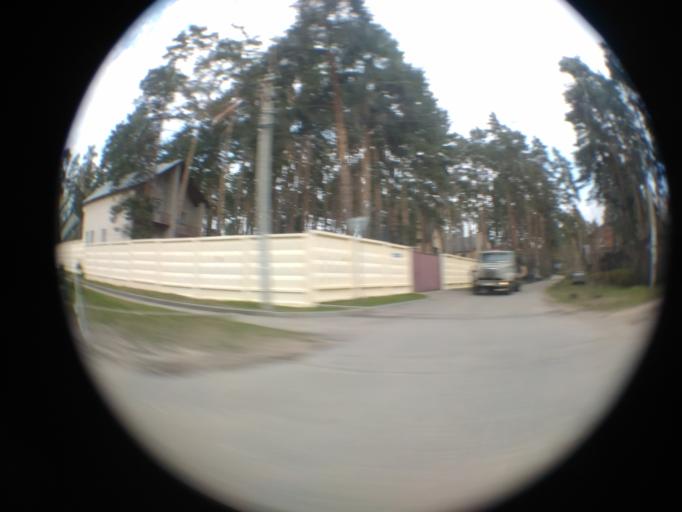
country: RU
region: Moskovskaya
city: Zhukovskiy
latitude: 55.5919
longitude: 38.1474
